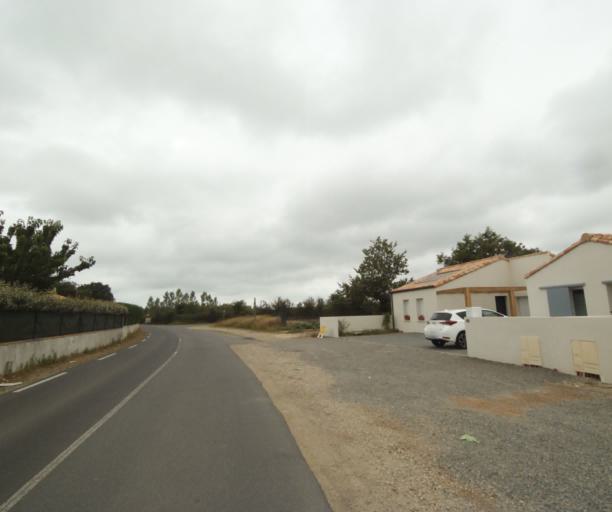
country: FR
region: Pays de la Loire
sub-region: Departement de la Vendee
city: Chateau-d'Olonne
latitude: 46.5078
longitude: -1.7475
